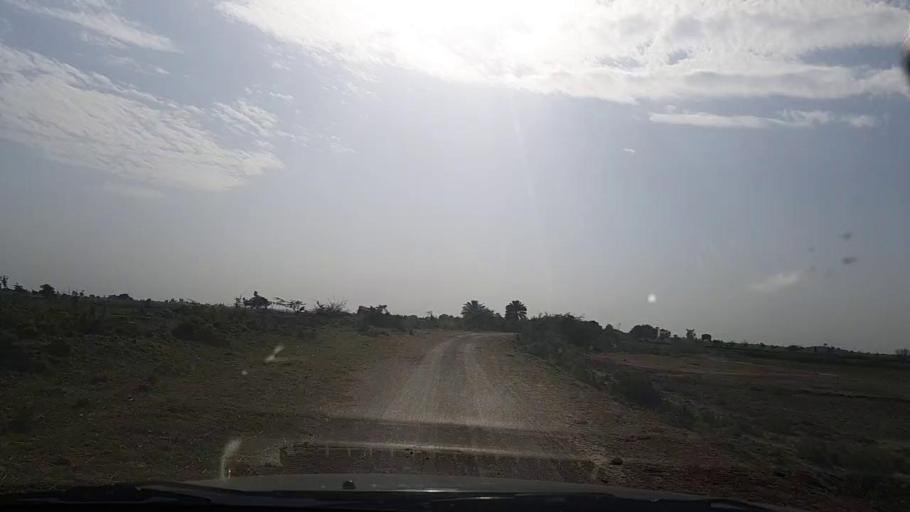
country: PK
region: Sindh
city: Mirpur Batoro
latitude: 24.5556
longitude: 68.1862
